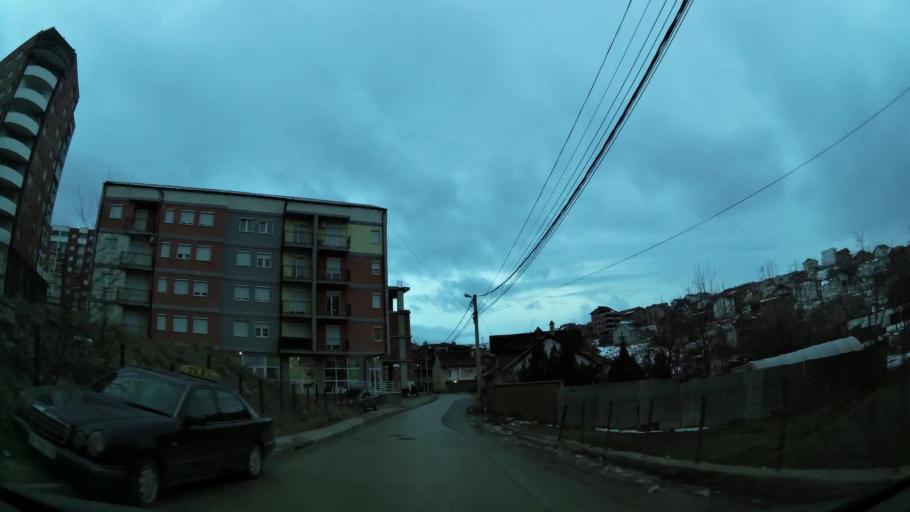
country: XK
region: Pristina
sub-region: Komuna e Prishtines
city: Pristina
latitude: 42.6429
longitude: 21.1676
